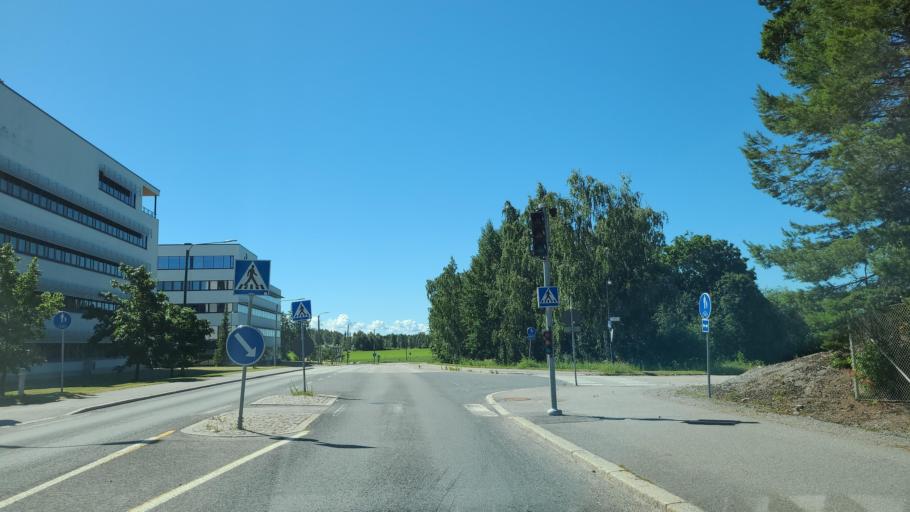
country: FI
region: Ostrobothnia
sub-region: Vaasa
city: Ristinummi
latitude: 63.0579
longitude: 21.7318
